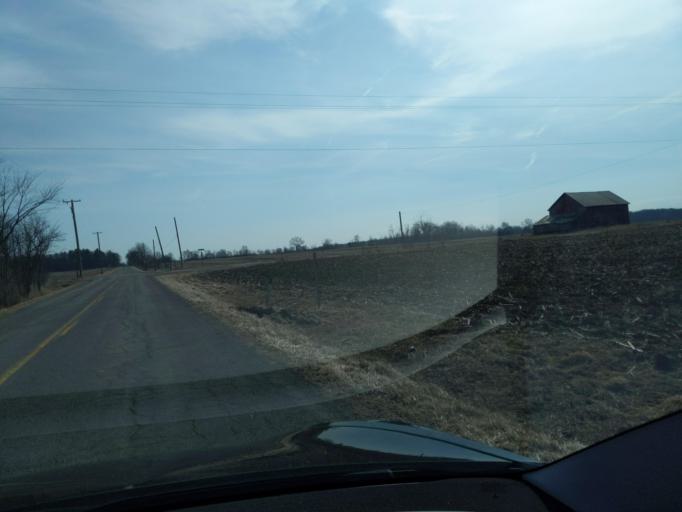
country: US
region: Michigan
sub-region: Ingham County
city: Williamston
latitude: 42.6585
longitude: -84.3419
